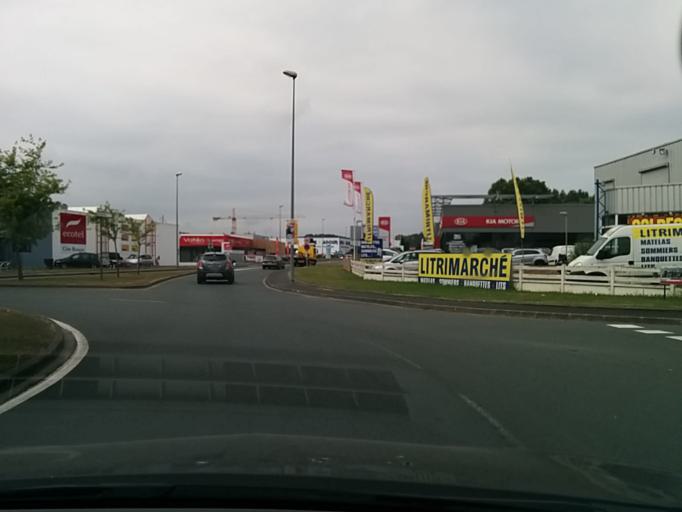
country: FR
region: Aquitaine
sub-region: Departement des Pyrenees-Atlantiques
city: Anglet
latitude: 43.4651
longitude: -1.4997
